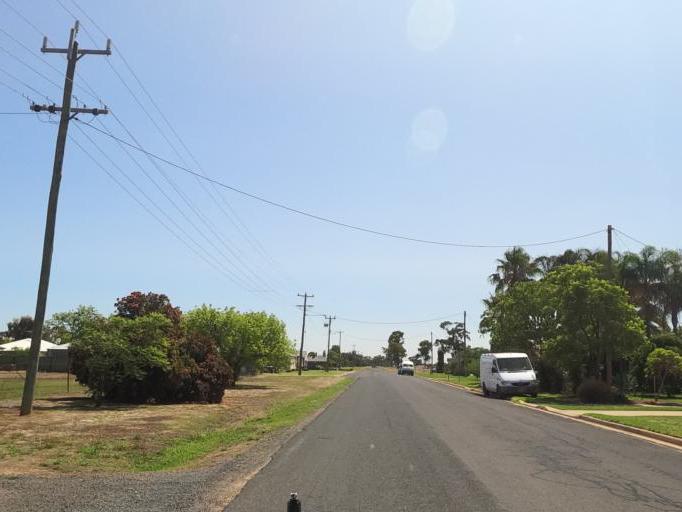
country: AU
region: New South Wales
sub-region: Corowa Shire
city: Mulwala
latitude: -35.9851
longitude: 145.9989
